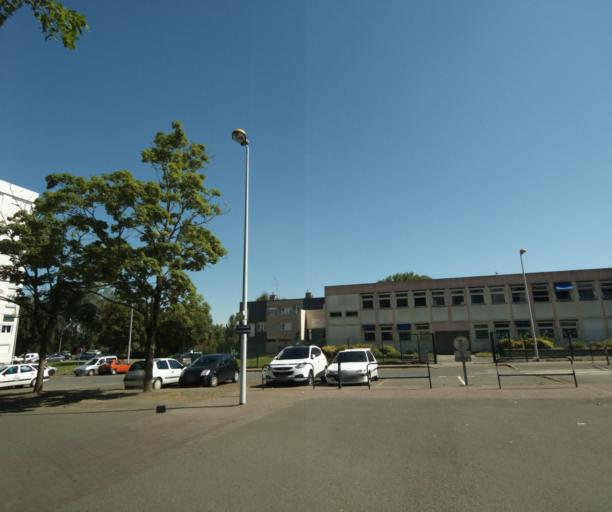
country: FR
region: Pays de la Loire
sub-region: Departement de la Mayenne
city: Laval
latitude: 48.0575
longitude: -0.7433
